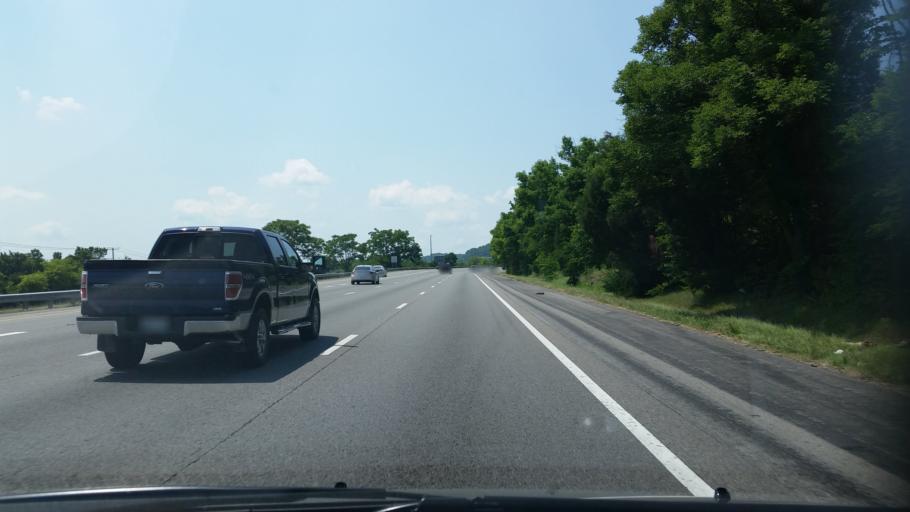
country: US
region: Tennessee
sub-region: Williamson County
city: Brentwood
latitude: 36.0520
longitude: -86.7756
